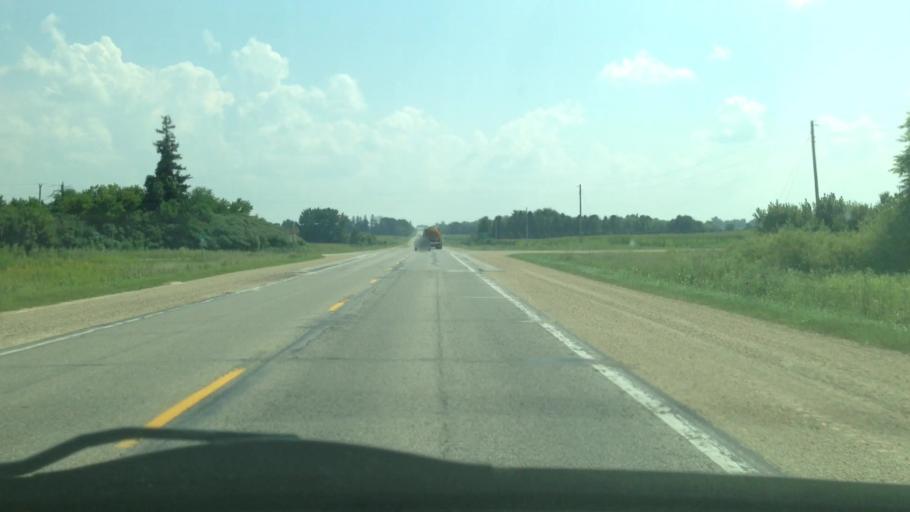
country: US
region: Iowa
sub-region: Chickasaw County
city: New Hampton
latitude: 43.2137
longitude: -92.2986
